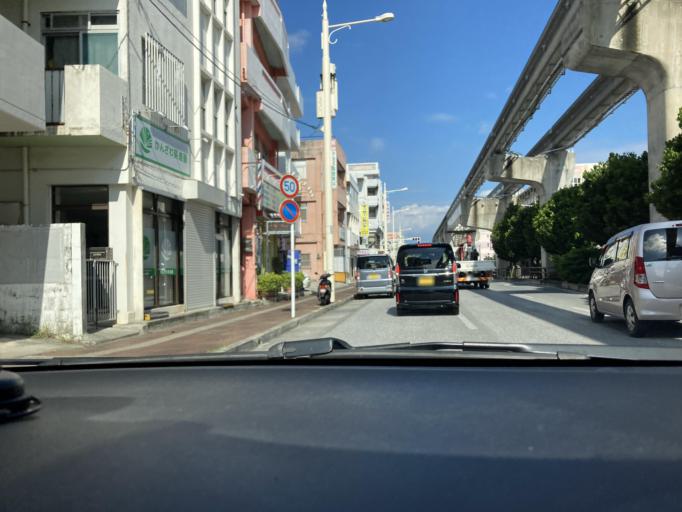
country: JP
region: Okinawa
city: Naha-shi
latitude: 26.2298
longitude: 127.7068
